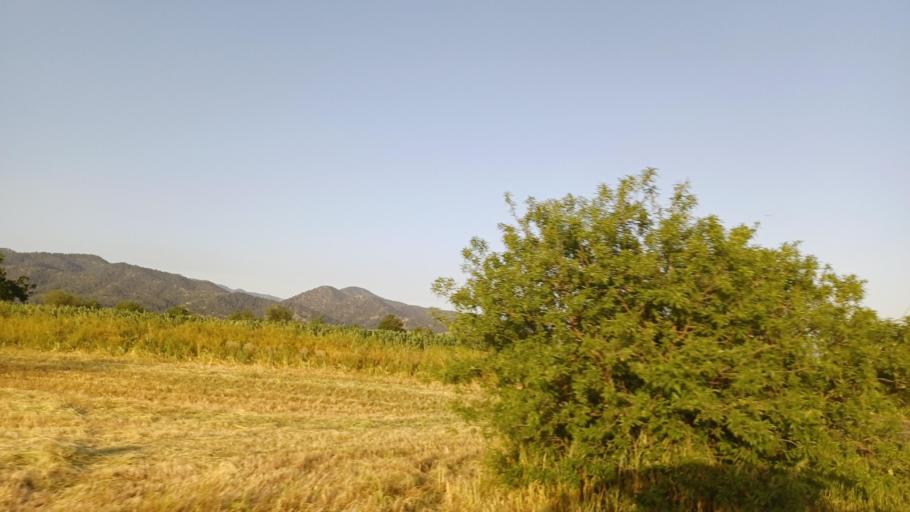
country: CY
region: Lefkosia
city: Astromeritis
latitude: 35.0775
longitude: 33.0189
